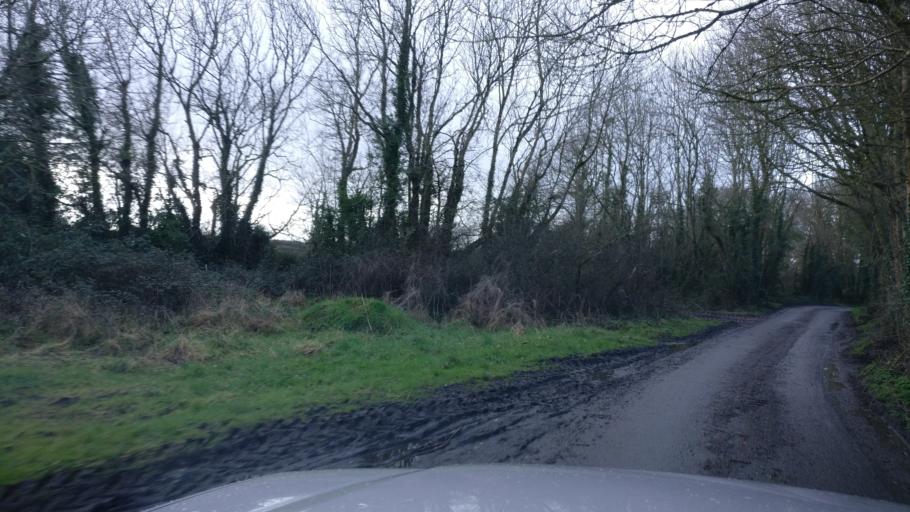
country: IE
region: Connaught
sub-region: County Galway
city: Oranmore
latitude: 53.2617
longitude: -8.8860
